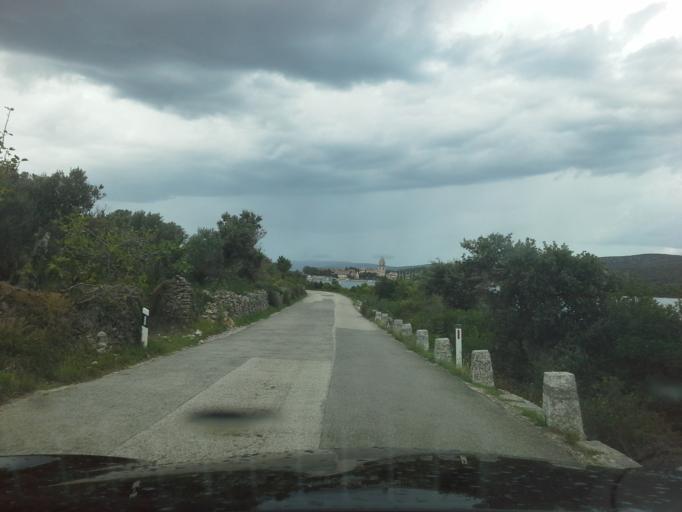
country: HR
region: Primorsko-Goranska
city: Mali Losinj
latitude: 44.6856
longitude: 14.3941
